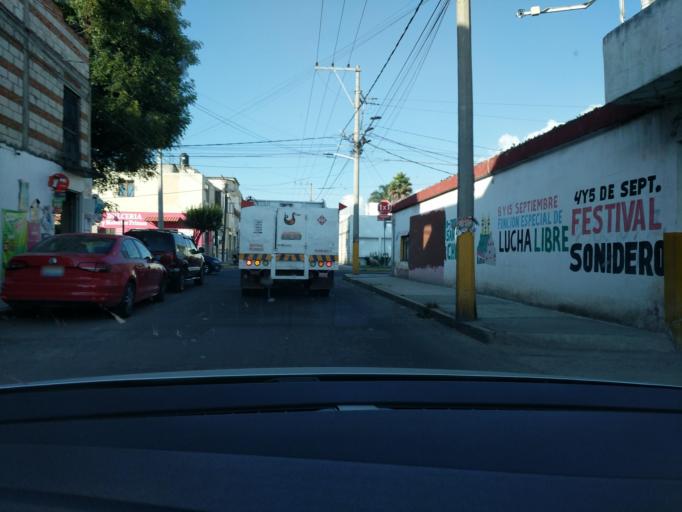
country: MX
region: Puebla
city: Cholula
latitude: 19.0554
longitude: -98.3121
